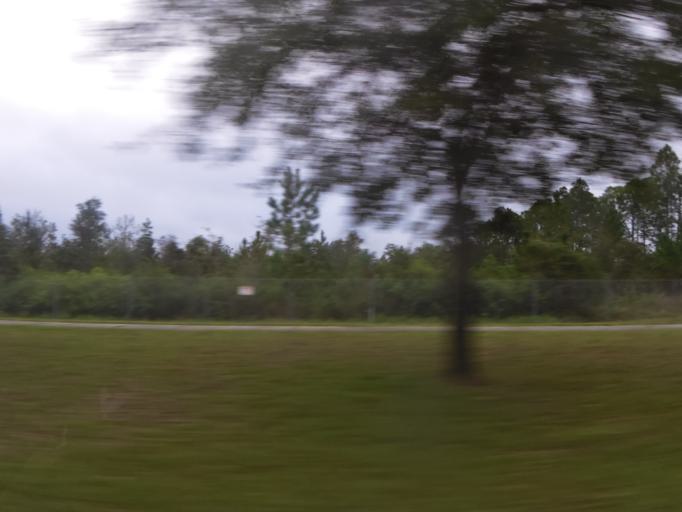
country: US
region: Florida
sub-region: Duval County
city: Baldwin
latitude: 30.2408
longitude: -81.8831
